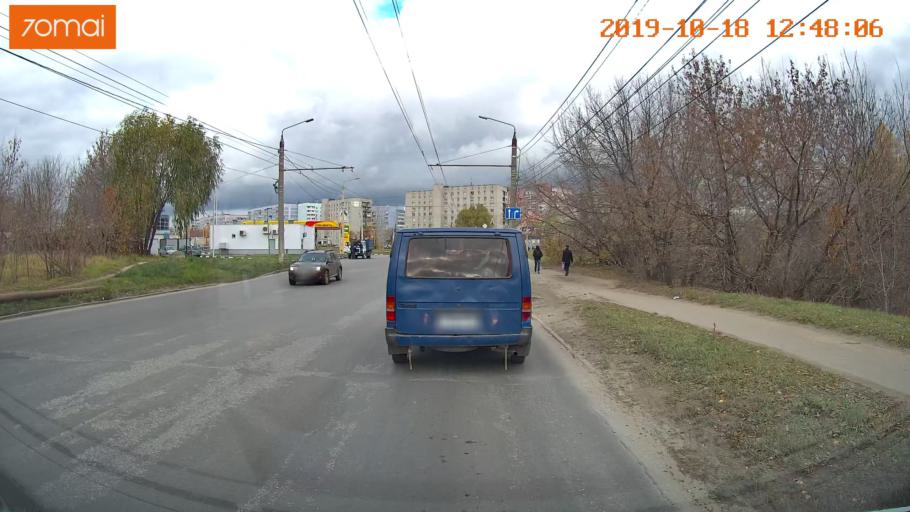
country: RU
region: Rjazan
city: Ryazan'
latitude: 54.6588
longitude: 39.6634
